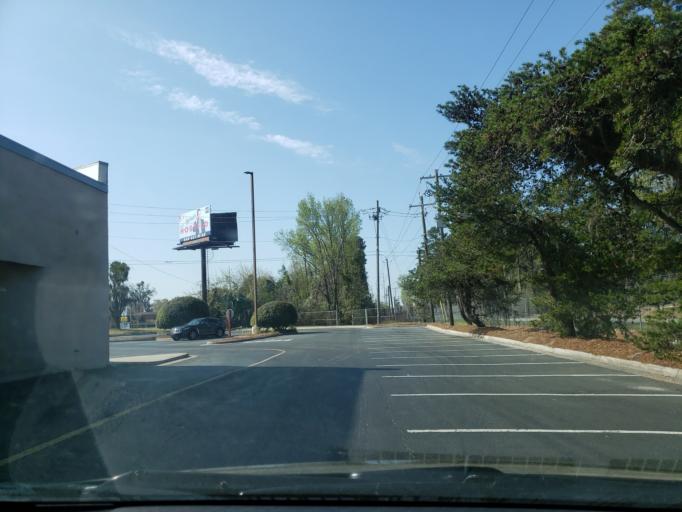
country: US
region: Georgia
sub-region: Chatham County
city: Montgomery
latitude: 32.0025
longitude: -81.1260
